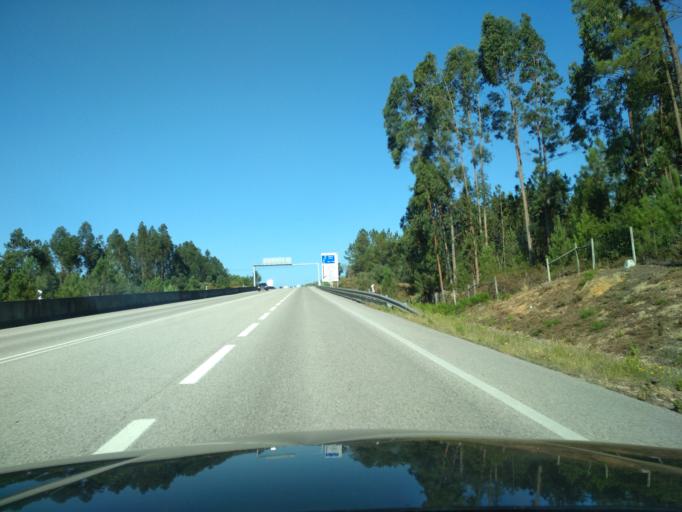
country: PT
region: Leiria
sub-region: Pombal
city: Lourical
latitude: 39.9884
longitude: -8.7752
